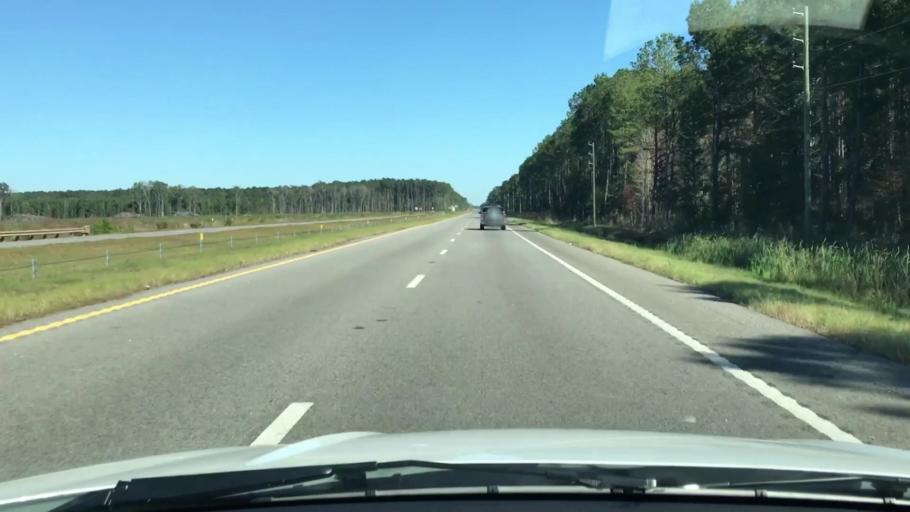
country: US
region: South Carolina
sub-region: Colleton County
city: Walterboro
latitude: 32.7616
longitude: -80.5231
